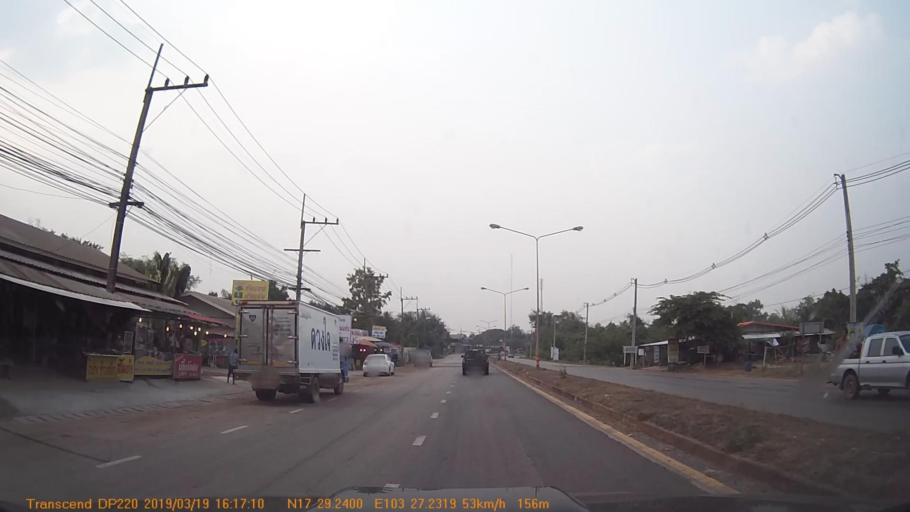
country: TH
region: Sakon Nakhon
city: Sawang Daen Din
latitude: 17.4878
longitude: 103.4537
